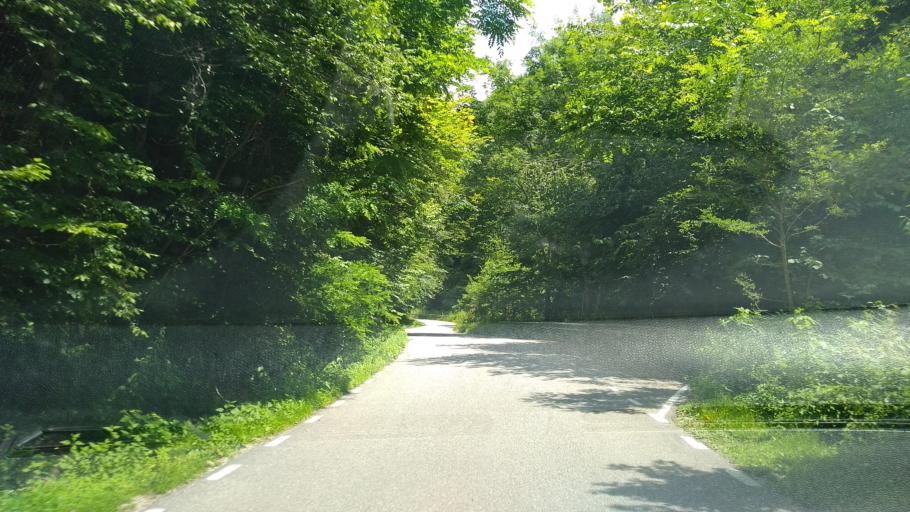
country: RO
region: Hunedoara
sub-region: Comuna Orastioara de Sus
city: Orastioara de Sus
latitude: 45.6216
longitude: 23.2908
